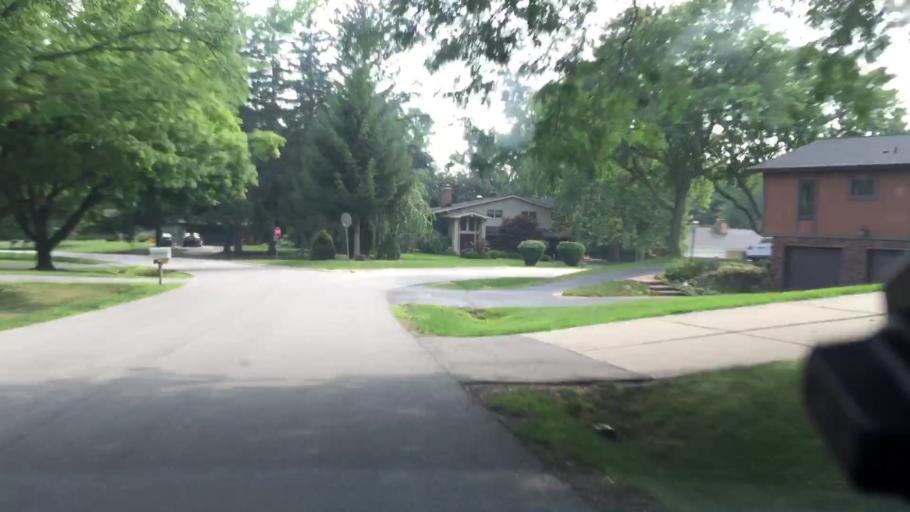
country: US
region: Michigan
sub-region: Oakland County
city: Sylvan Lake
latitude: 42.6008
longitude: -83.2930
